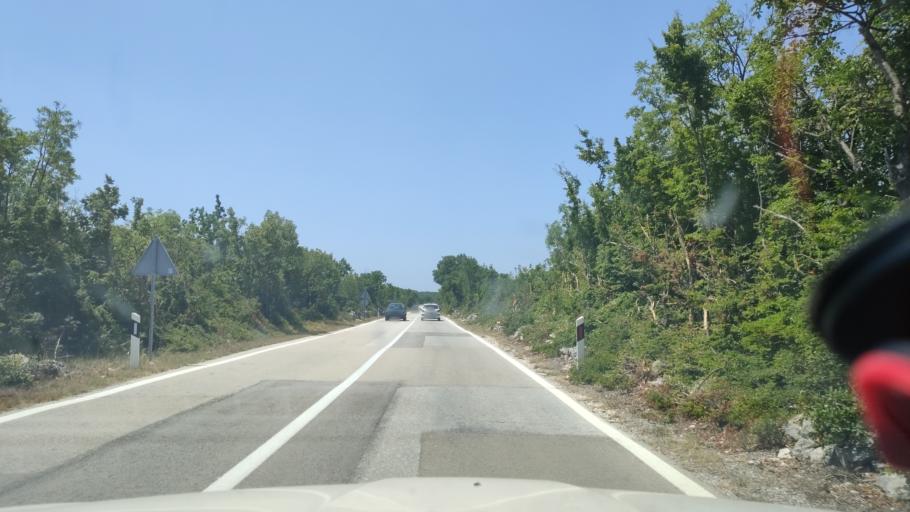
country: HR
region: Sibensko-Kniniska
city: Kistanje
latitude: 43.9730
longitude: 15.9118
